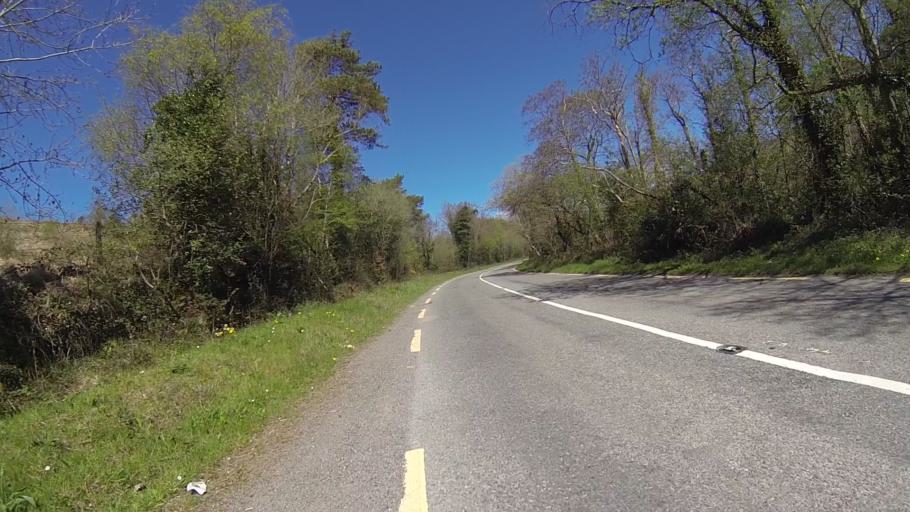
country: IE
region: Munster
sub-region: Ciarrai
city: Kenmare
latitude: 51.8958
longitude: -9.6020
